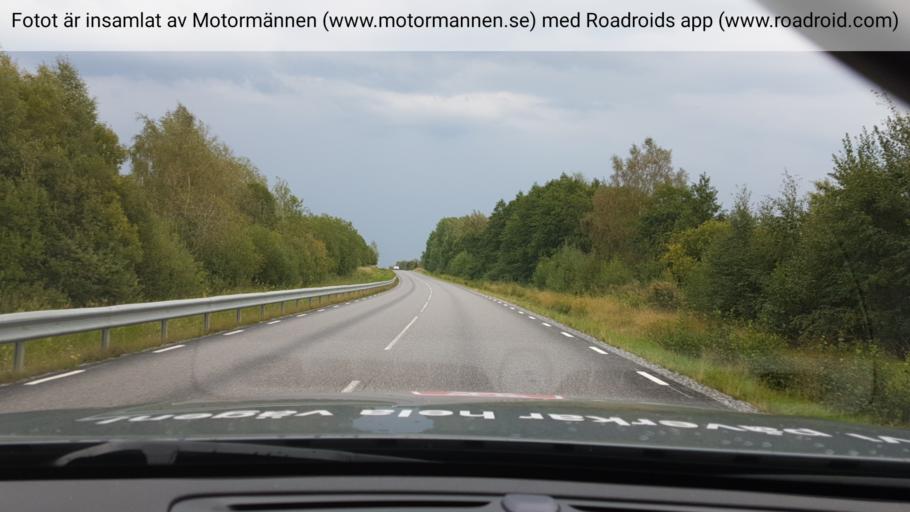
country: SE
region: Stockholm
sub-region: Upplands-Bro Kommun
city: Bro
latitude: 59.5256
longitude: 17.5853
